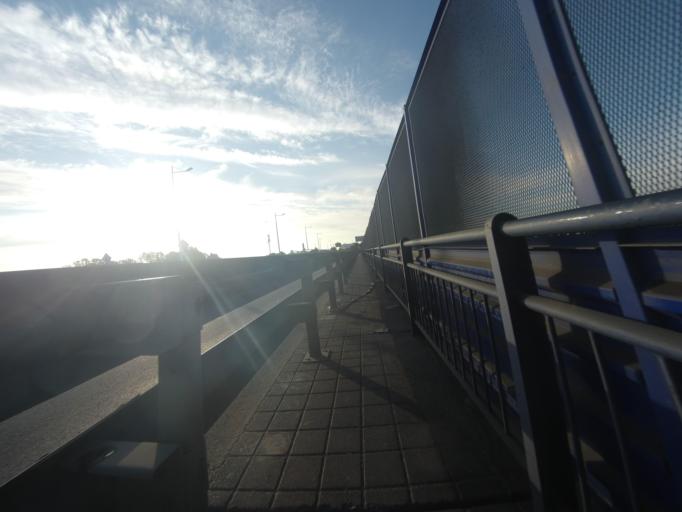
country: ES
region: Andalusia
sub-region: Provincia de Huelva
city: Punta Umbria
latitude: 37.2061
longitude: -6.9371
